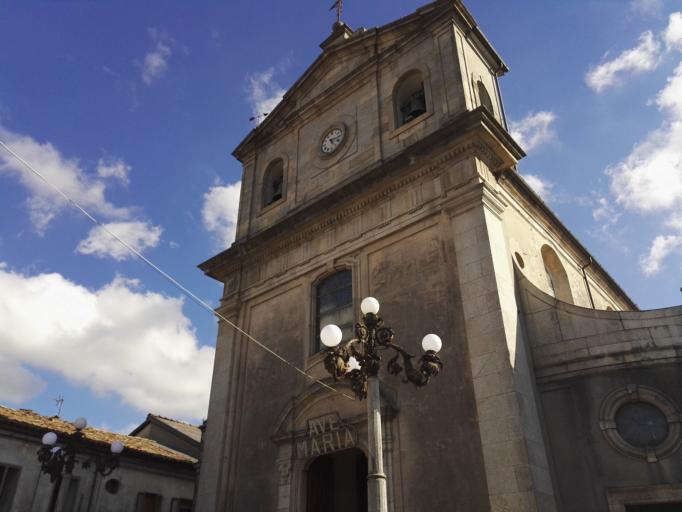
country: IT
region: Calabria
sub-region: Provincia di Vibo-Valentia
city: Serra San Bruno
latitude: 38.5758
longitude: 16.3294
